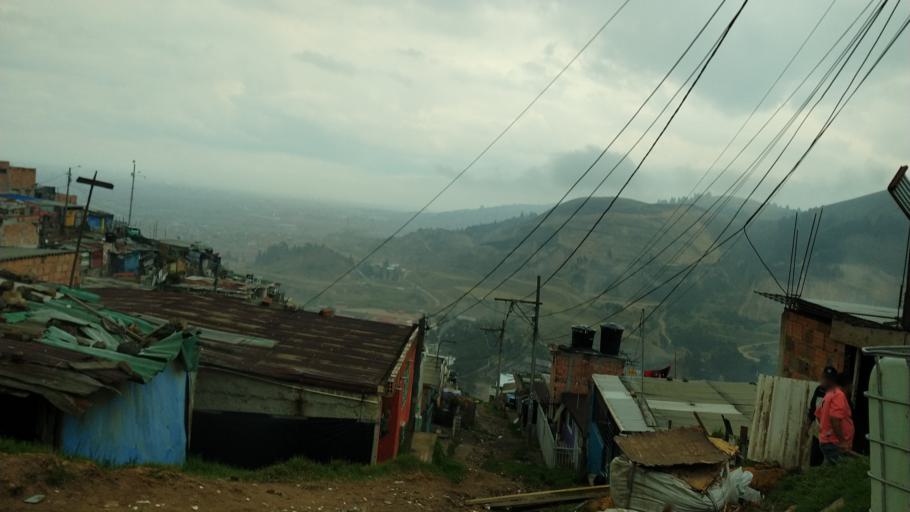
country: CO
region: Cundinamarca
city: Soacha
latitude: 4.5621
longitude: -74.2172
